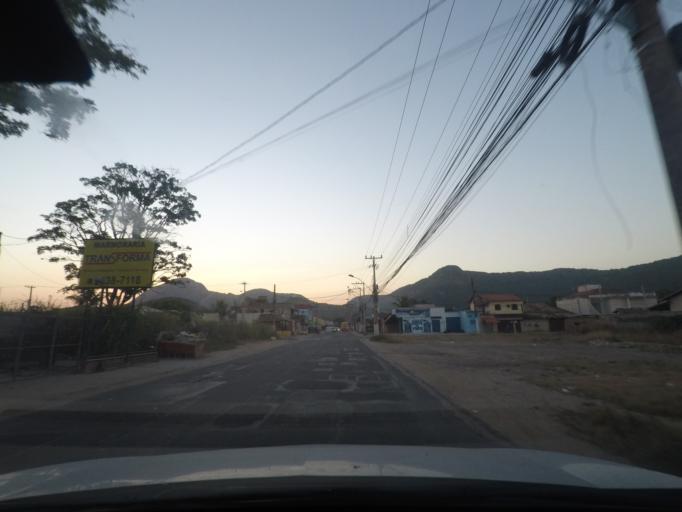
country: BR
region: Rio de Janeiro
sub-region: Niteroi
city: Niteroi
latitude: -22.9621
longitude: -42.9938
